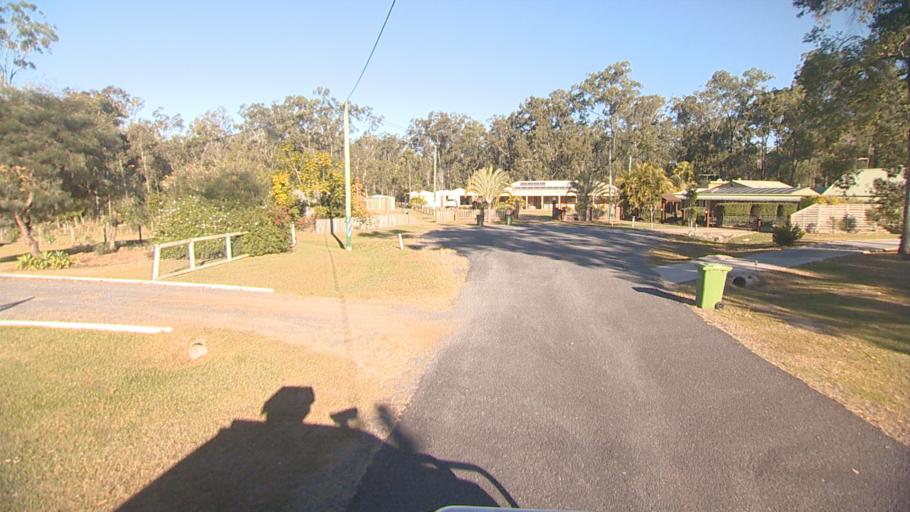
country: AU
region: Queensland
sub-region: Logan
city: North Maclean
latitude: -27.7479
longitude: 153.0202
